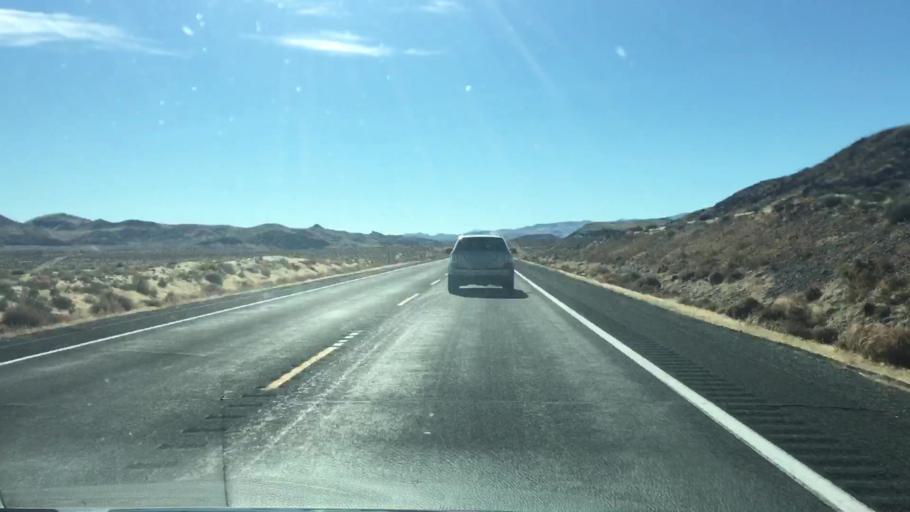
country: US
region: Nevada
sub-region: Lyon County
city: Silver Springs
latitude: 39.3162
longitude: -119.2505
